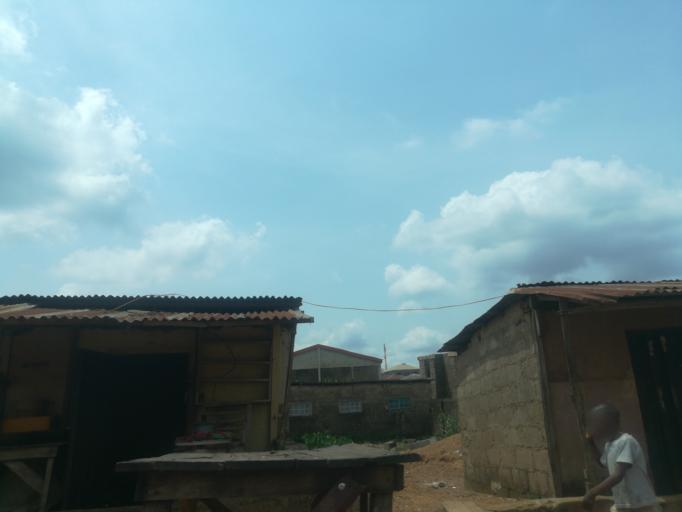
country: NG
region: Oyo
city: Moniya
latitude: 7.4513
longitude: 3.9556
